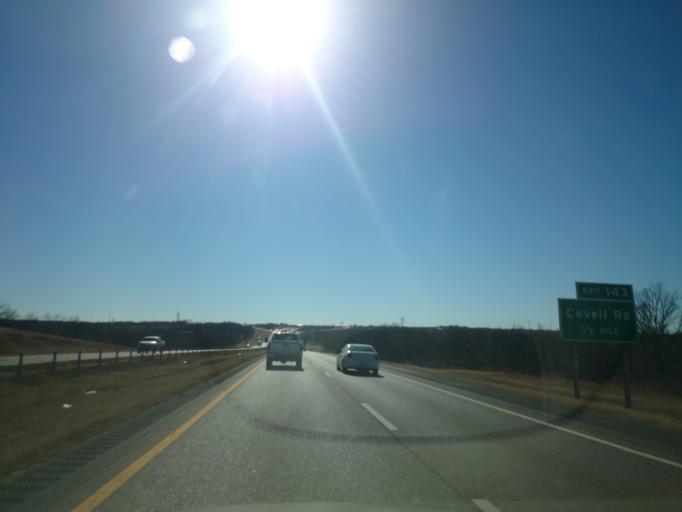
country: US
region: Oklahoma
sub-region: Oklahoma County
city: Edmond
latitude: 35.6949
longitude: -97.4163
